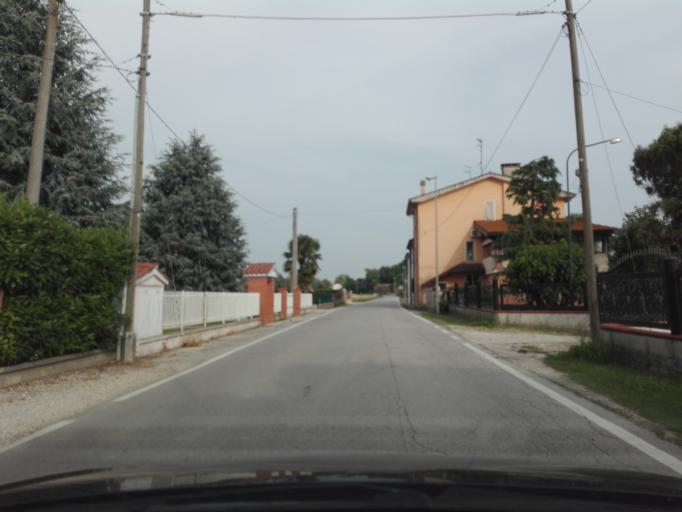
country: IT
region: Veneto
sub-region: Provincia di Rovigo
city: Adria
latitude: 45.0624
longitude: 11.9864
